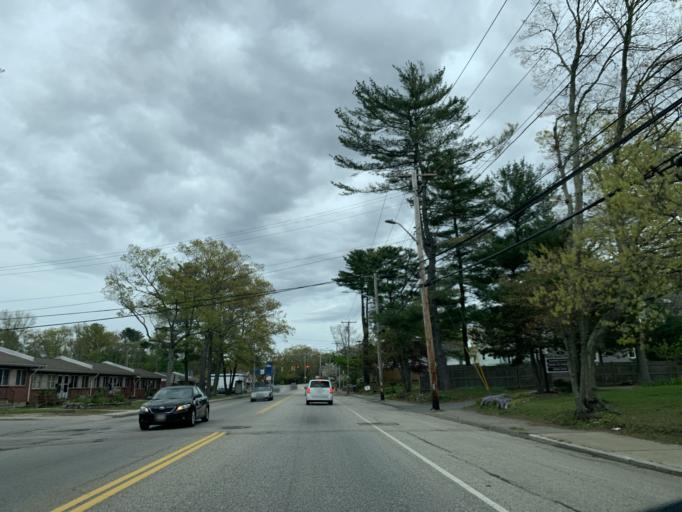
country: US
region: Massachusetts
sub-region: Bristol County
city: Attleboro
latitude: 41.9339
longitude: -71.3093
